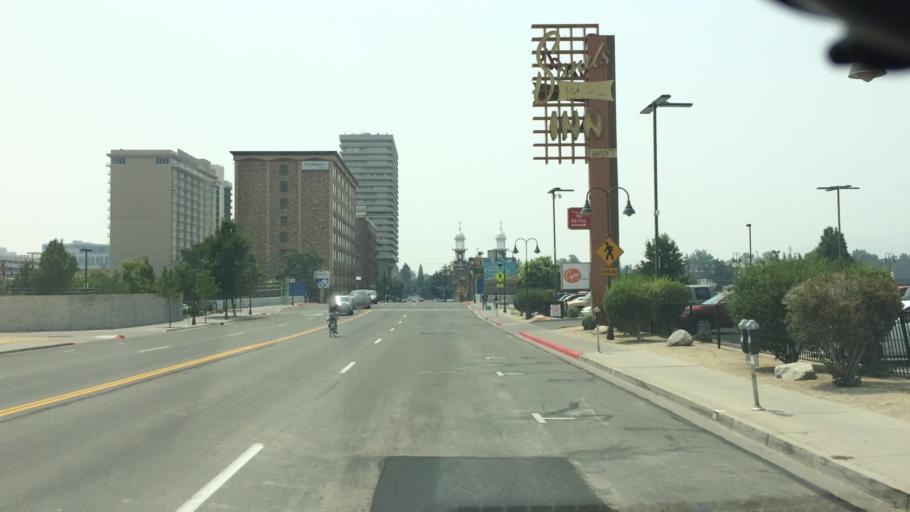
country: US
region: Nevada
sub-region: Washoe County
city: Reno
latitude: 39.5286
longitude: -119.8181
